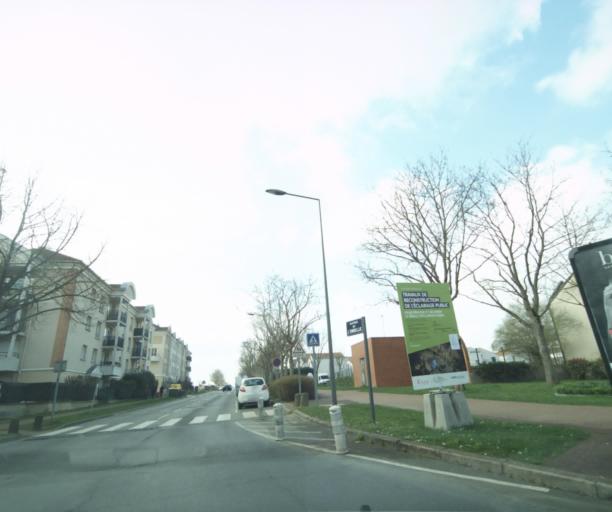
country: FR
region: Ile-de-France
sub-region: Departement du Val-d'Oise
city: Vaureal
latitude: 49.0472
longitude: 2.0309
